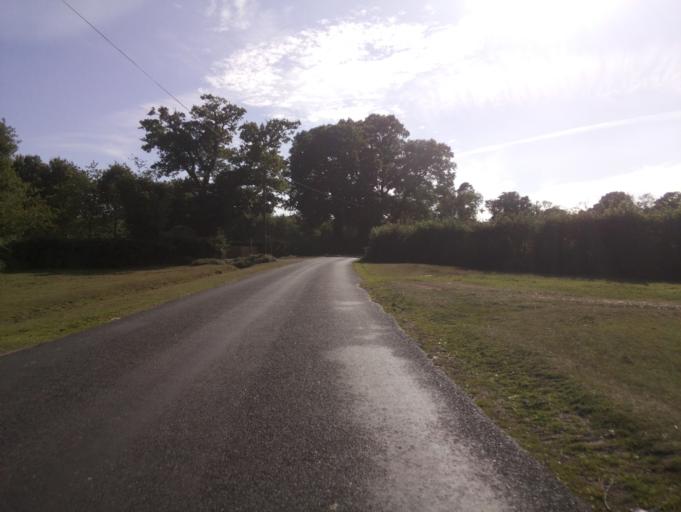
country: GB
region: England
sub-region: Hampshire
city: Cadnam
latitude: 50.9404
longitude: -1.6037
